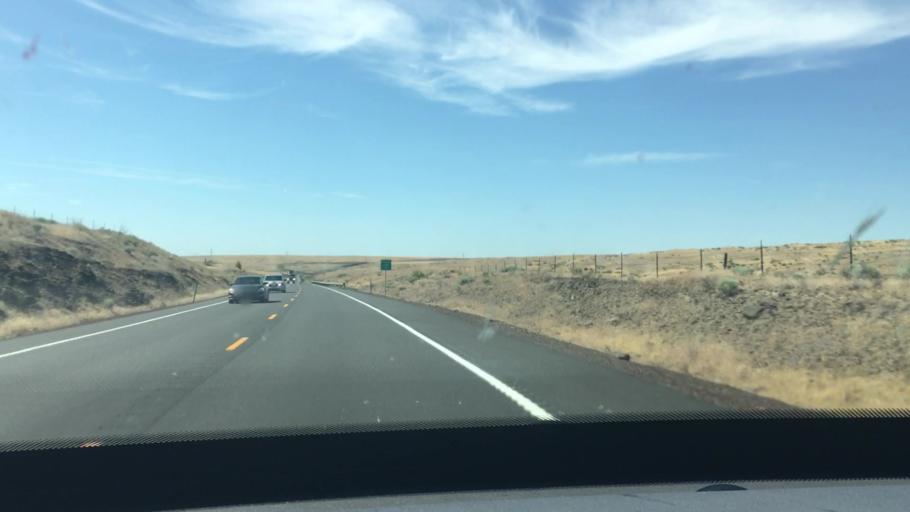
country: US
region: Oregon
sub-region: Sherman County
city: Moro
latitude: 45.2530
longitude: -120.7291
